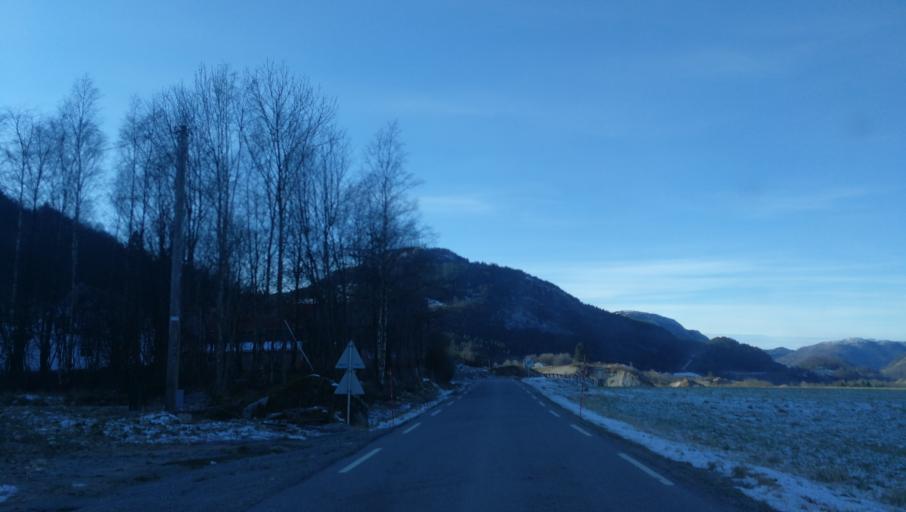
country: NO
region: Rogaland
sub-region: Hjelmeland
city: Hjelmelandsvagen
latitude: 59.1278
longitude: 6.2681
